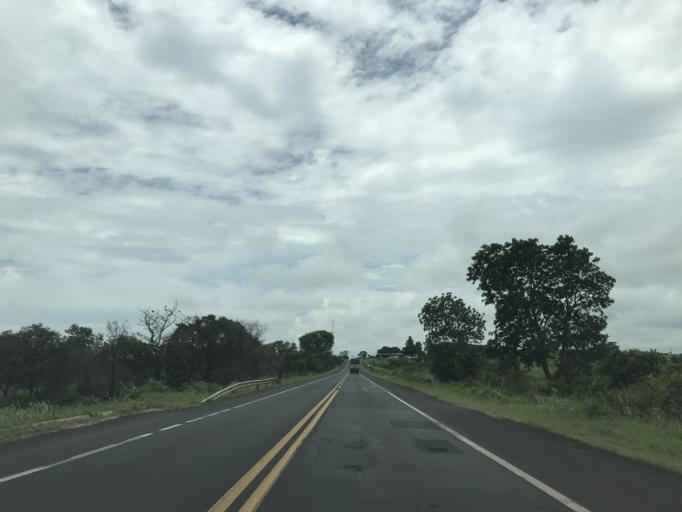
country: BR
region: Minas Gerais
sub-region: Frutal
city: Frutal
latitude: -19.8468
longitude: -48.9633
